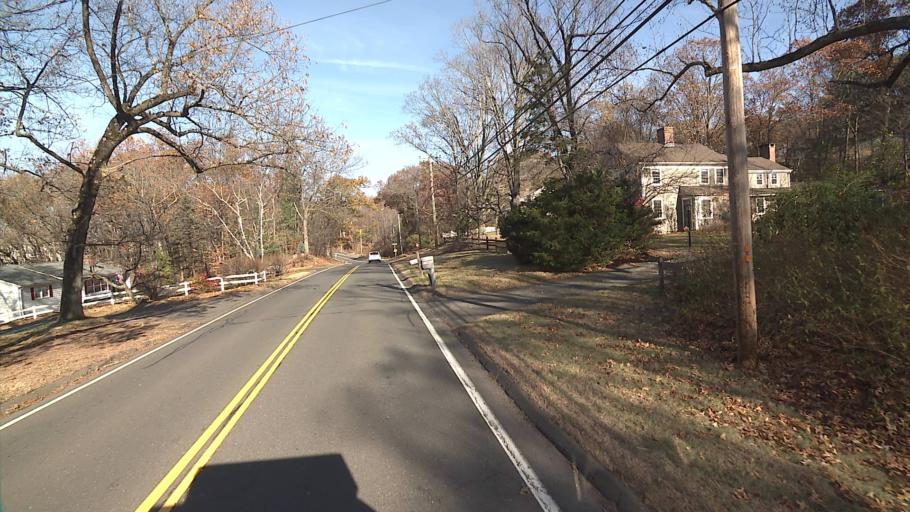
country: US
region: Connecticut
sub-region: Hartford County
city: Glastonbury Center
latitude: 41.6495
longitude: -72.6045
